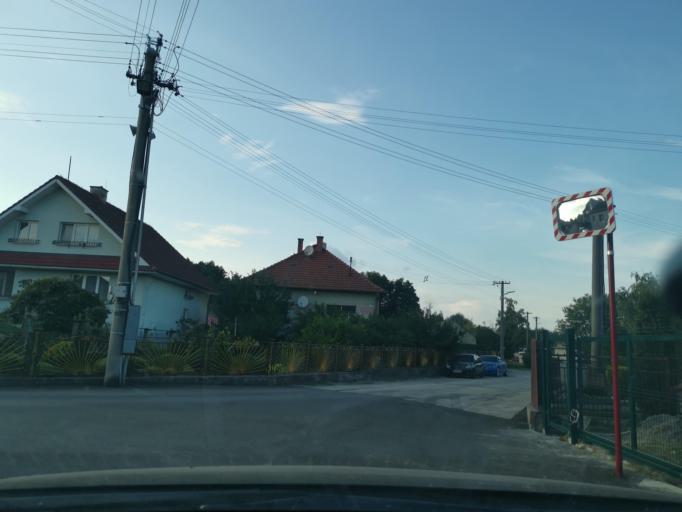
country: SK
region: Trnavsky
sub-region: Okres Senica
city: Senica
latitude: 48.6560
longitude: 17.2690
